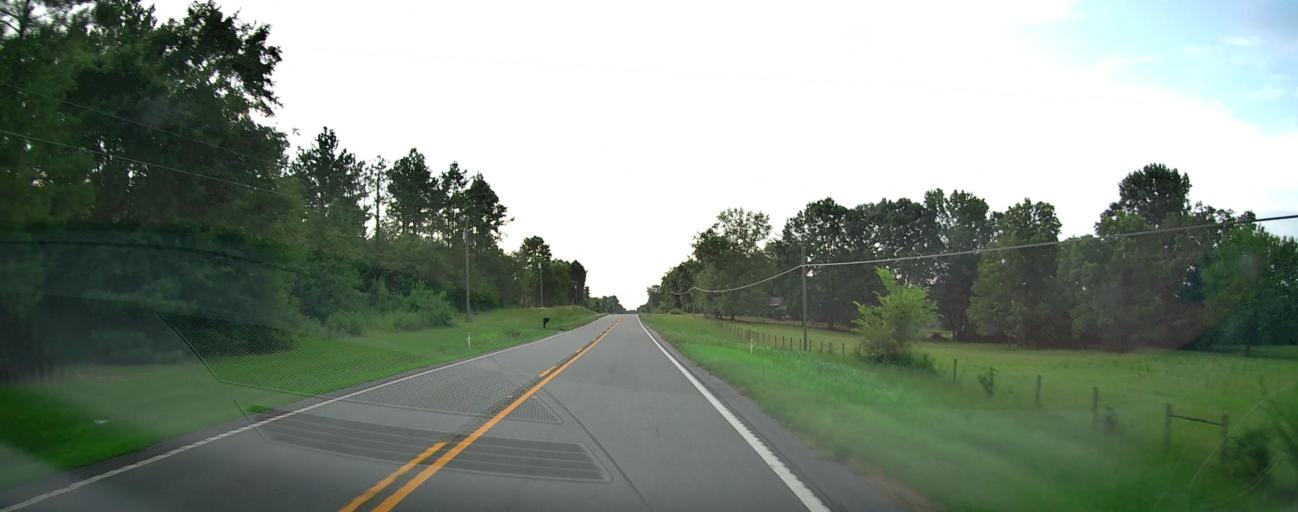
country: US
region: Georgia
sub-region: Taylor County
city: Reynolds
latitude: 32.6023
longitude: -84.0947
